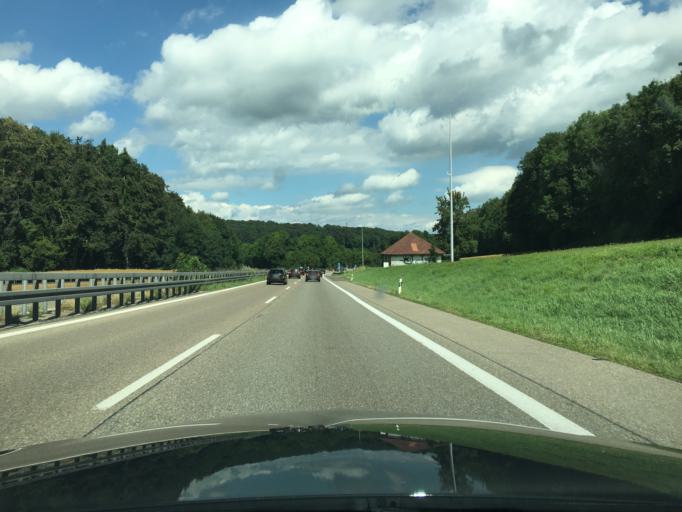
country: DE
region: Baden-Wuerttemberg
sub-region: Regierungsbezirk Stuttgart
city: Hohenstadt
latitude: 48.5407
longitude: 9.6491
